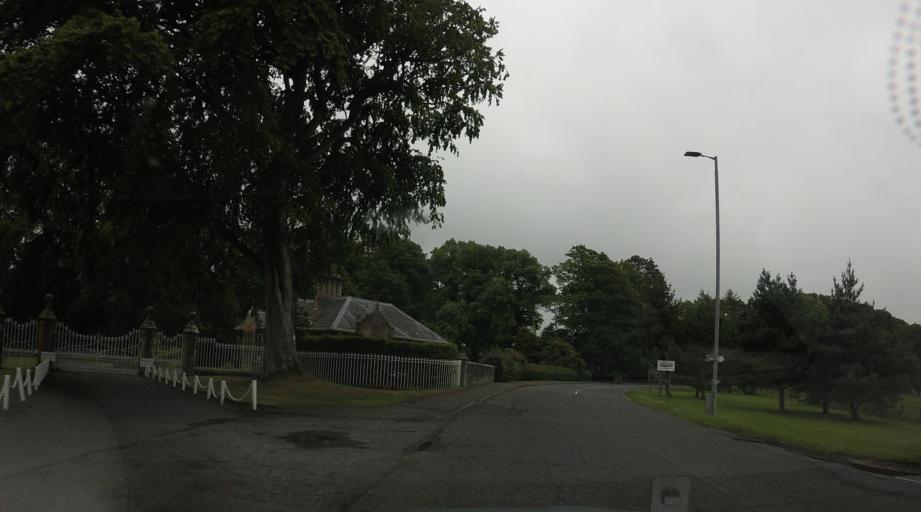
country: GB
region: Scotland
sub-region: South Ayrshire
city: Ayr
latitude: 55.4258
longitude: -4.6388
